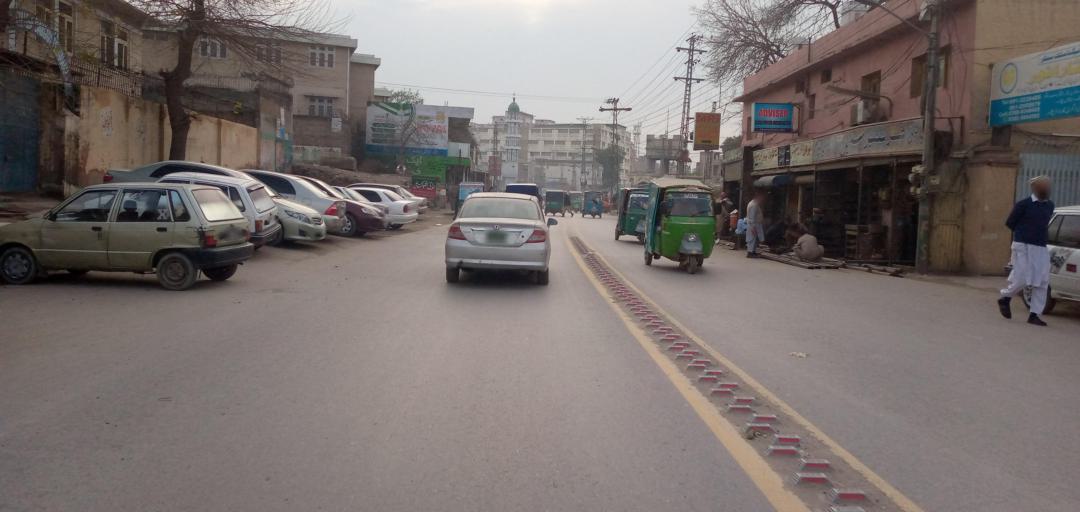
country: PK
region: Khyber Pakhtunkhwa
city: Peshawar
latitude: 34.0060
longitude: 71.5622
